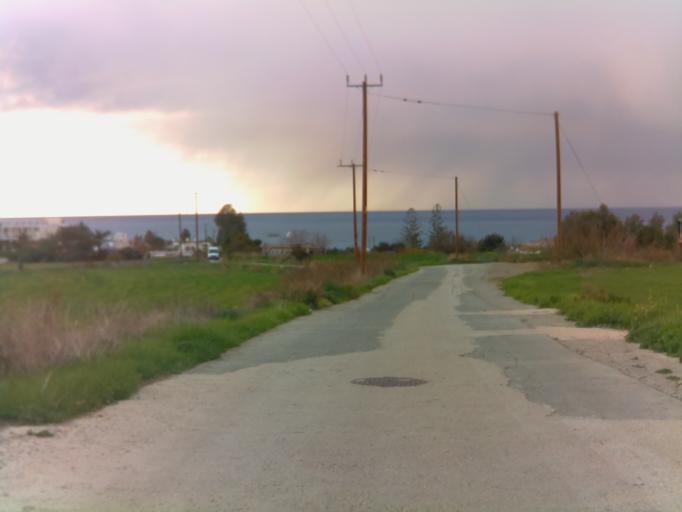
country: CY
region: Pafos
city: Kissonerga
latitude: 34.8117
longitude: 32.4006
